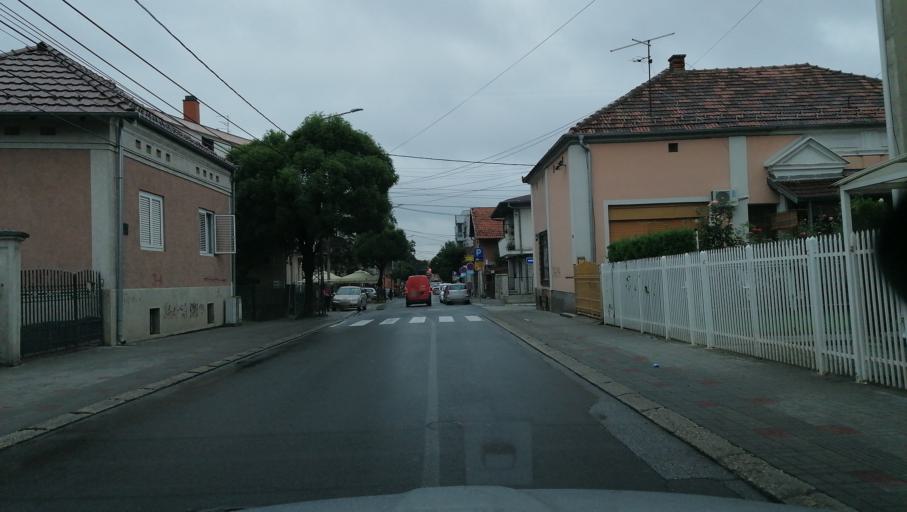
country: RS
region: Central Serbia
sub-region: Rasinski Okrug
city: Krusevac
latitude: 43.5804
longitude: 21.3227
